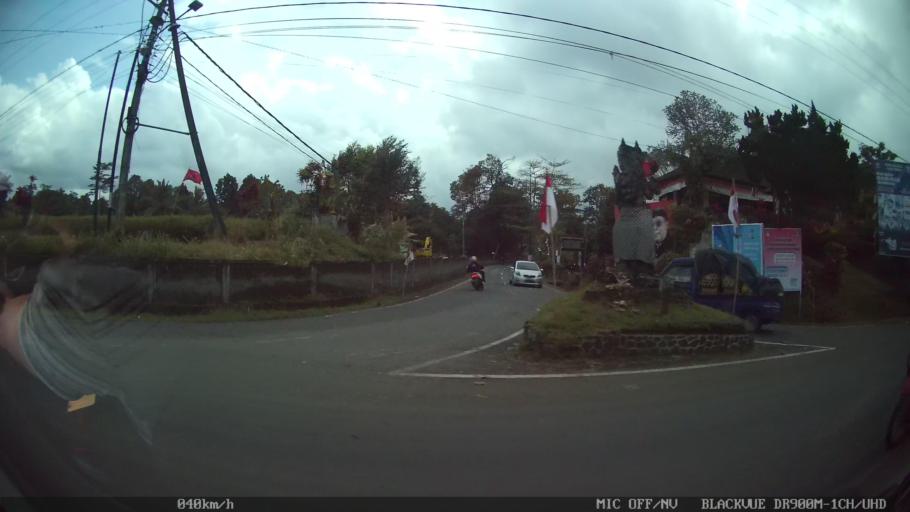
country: ID
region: Bali
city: Pohgending Kawan
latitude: -8.4536
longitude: 115.1387
